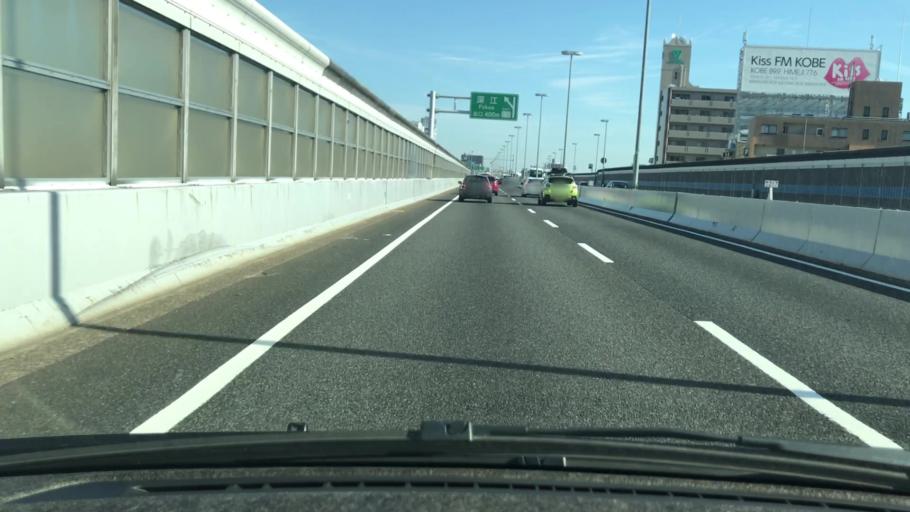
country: JP
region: Hyogo
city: Ashiya
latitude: 34.7159
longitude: 135.2821
